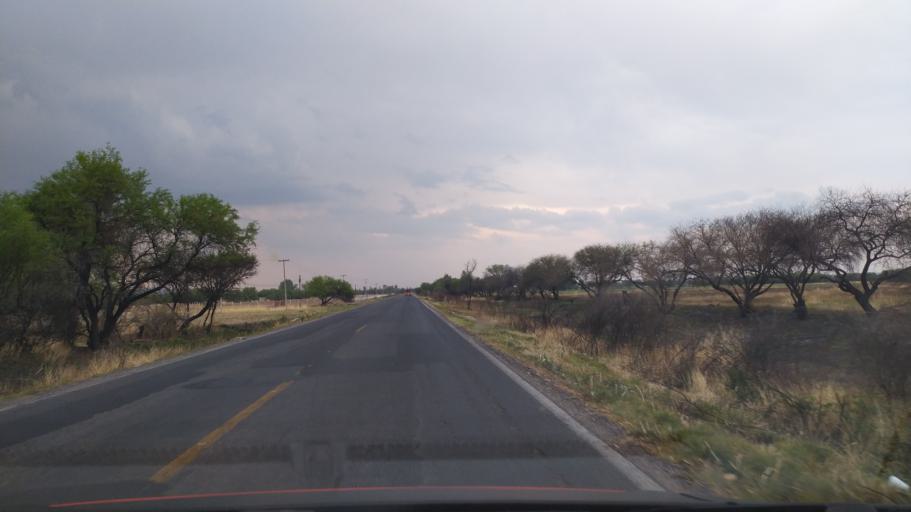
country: MX
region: Guanajuato
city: Ciudad Manuel Doblado
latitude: 20.7749
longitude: -101.9117
